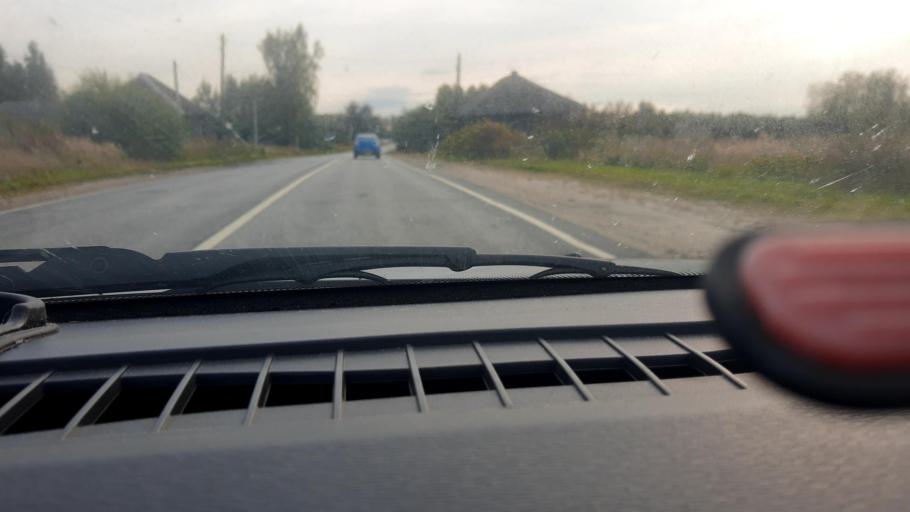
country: RU
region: Nizjnij Novgorod
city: Krasnyye Baki
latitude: 57.0150
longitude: 45.1156
